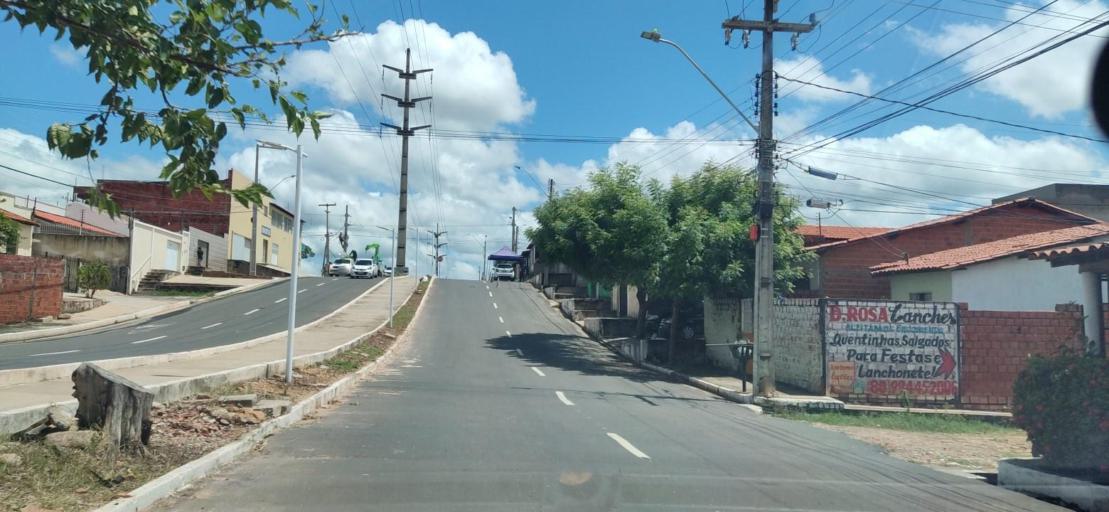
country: BR
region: Piaui
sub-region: Teresina
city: Teresina
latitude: -5.0661
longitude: -42.7514
